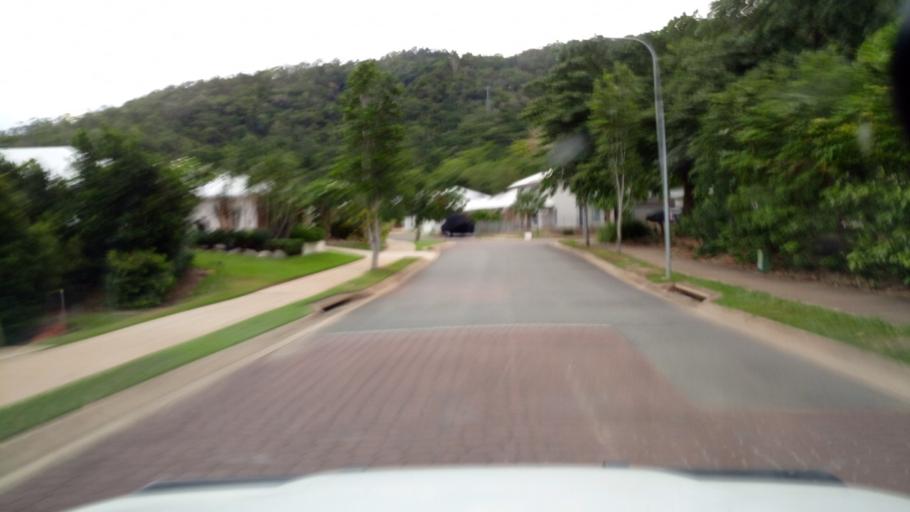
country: AU
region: Queensland
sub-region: Cairns
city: Redlynch
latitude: -16.8426
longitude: 145.6887
